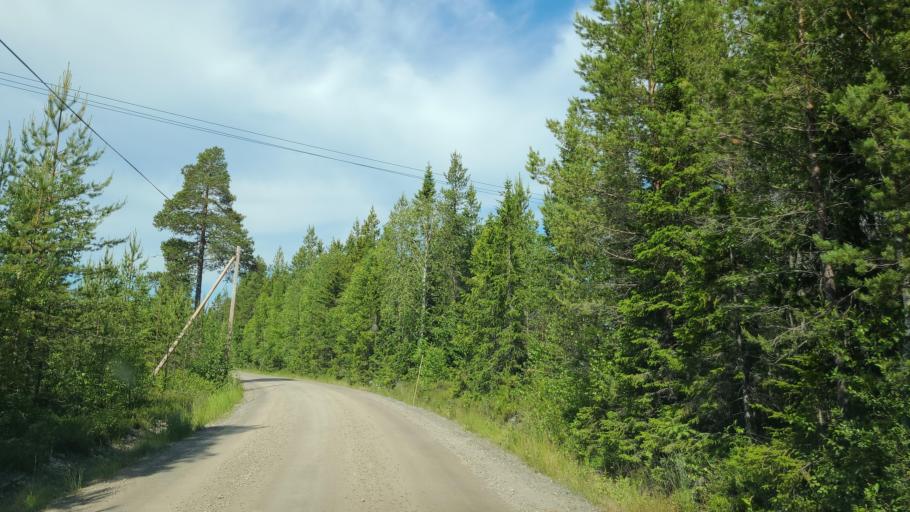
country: SE
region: Vaesterbotten
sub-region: Robertsfors Kommun
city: Robertsfors
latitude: 64.1546
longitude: 20.9481
